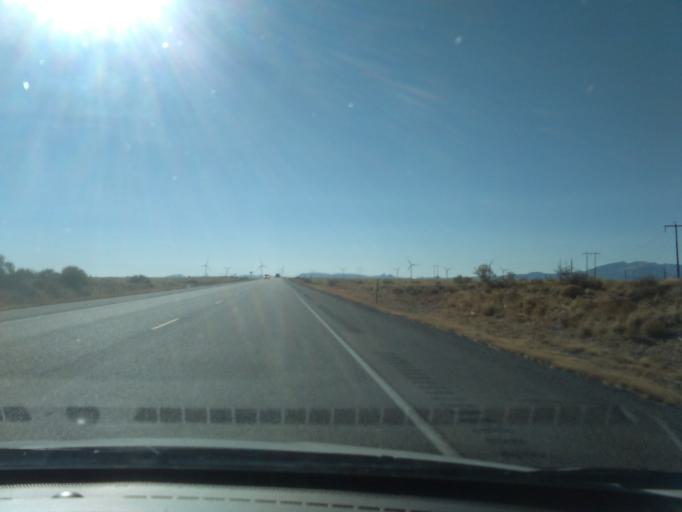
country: US
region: New Mexico
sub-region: Dona Ana County
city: Hatch
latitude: 32.5630
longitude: -107.4670
